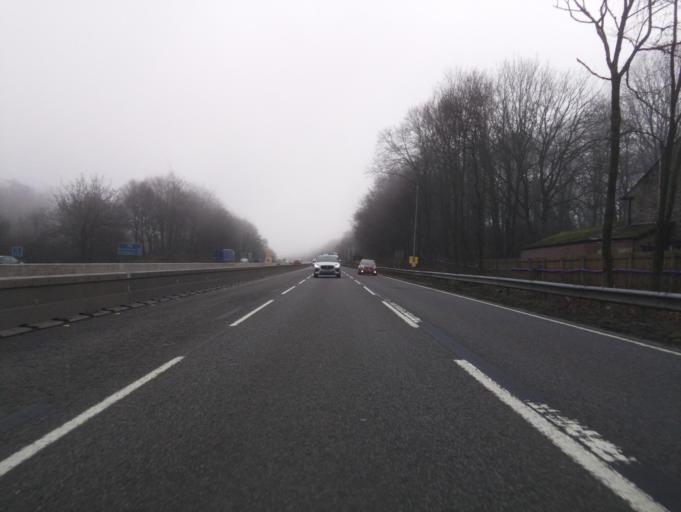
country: GB
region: England
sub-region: St. Helens
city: Billinge
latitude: 53.5257
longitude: -2.6982
